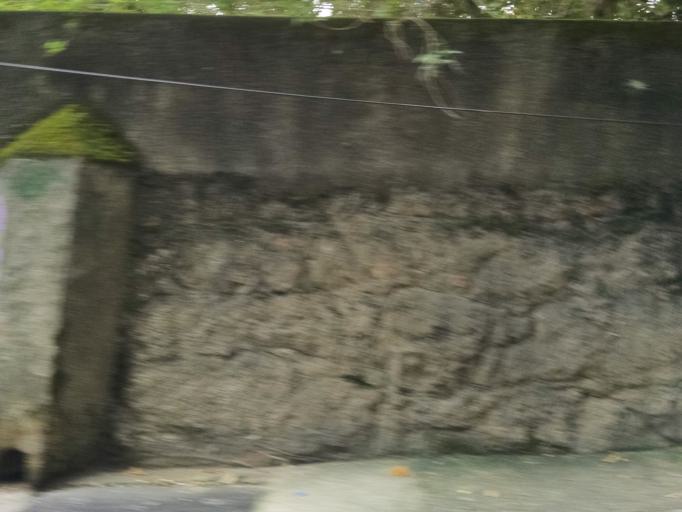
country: BR
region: Rio de Janeiro
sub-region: Rio De Janeiro
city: Rio de Janeiro
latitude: -22.9307
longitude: -43.1959
